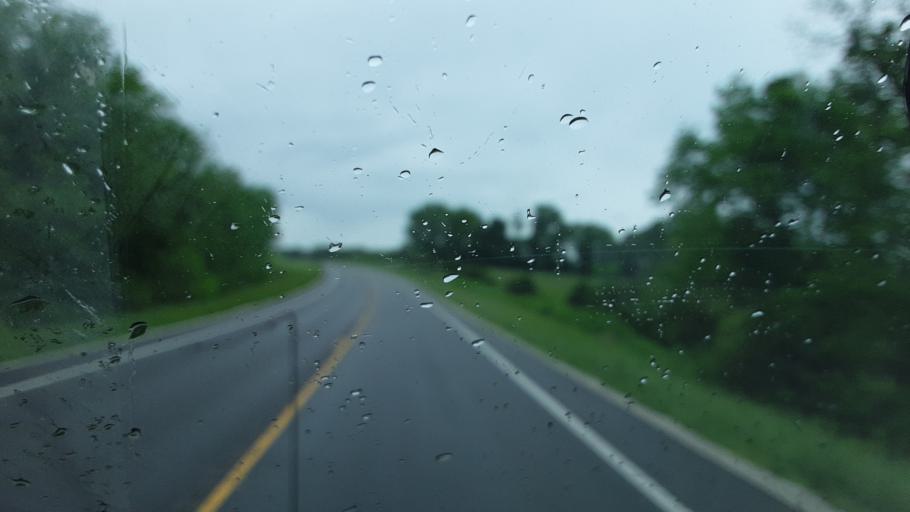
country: US
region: Missouri
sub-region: Monroe County
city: Paris
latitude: 39.4813
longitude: -92.1218
